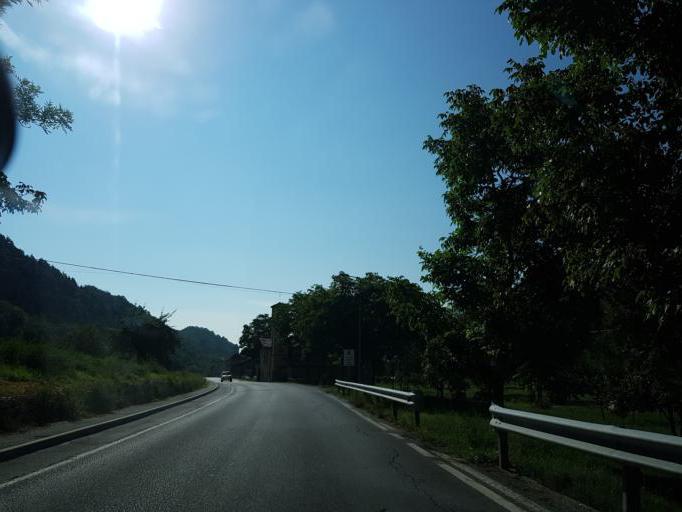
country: IT
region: Piedmont
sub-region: Provincia di Cuneo
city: San Damiano Macra
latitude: 44.4858
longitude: 7.2715
